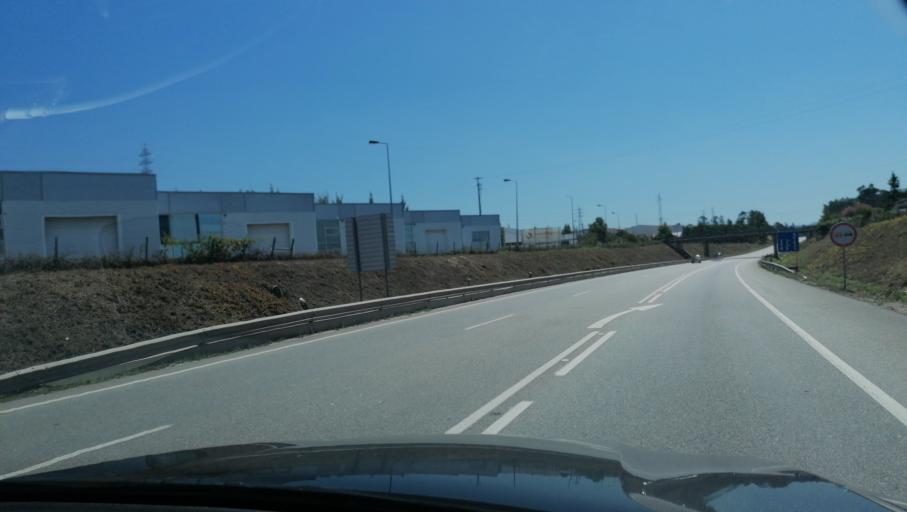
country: PT
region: Aveiro
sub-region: Agueda
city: Aguada de Cima
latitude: 40.5374
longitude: -8.4616
